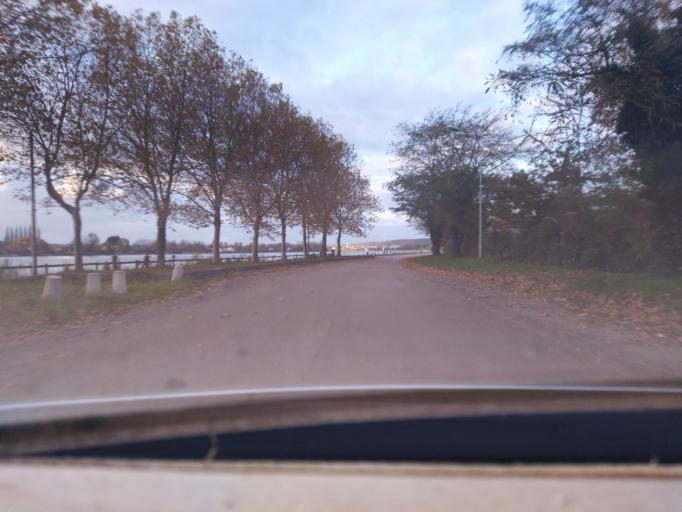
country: FR
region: Haute-Normandie
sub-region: Departement de la Seine-Maritime
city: Le Trait
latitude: 49.4591
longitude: 0.8192
